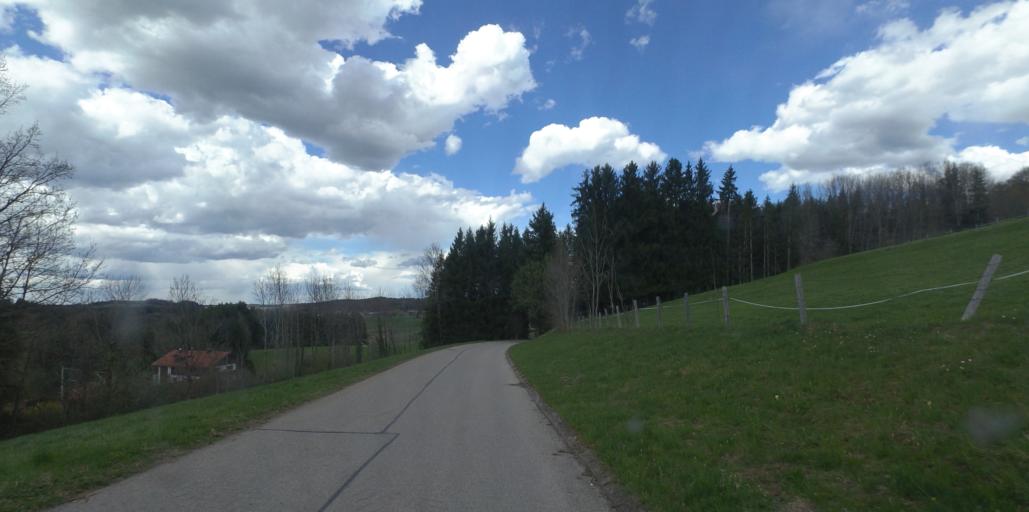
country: DE
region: Bavaria
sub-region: Upper Bavaria
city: Vachendorf
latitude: 47.8324
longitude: 12.6033
